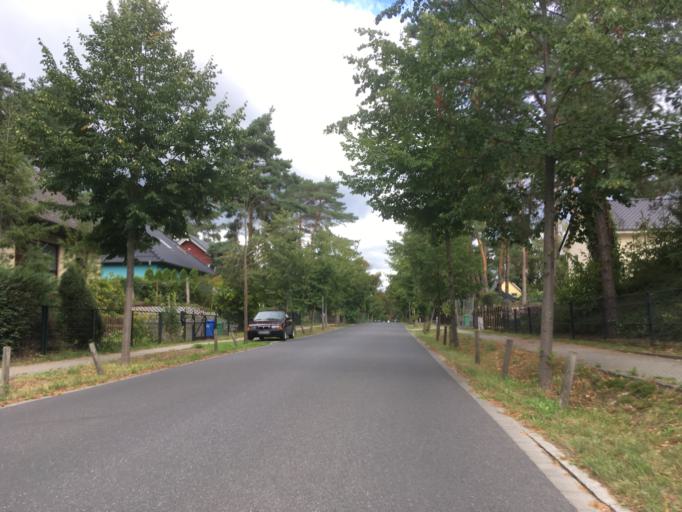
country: DE
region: Brandenburg
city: Wildau
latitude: 52.3124
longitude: 13.7015
